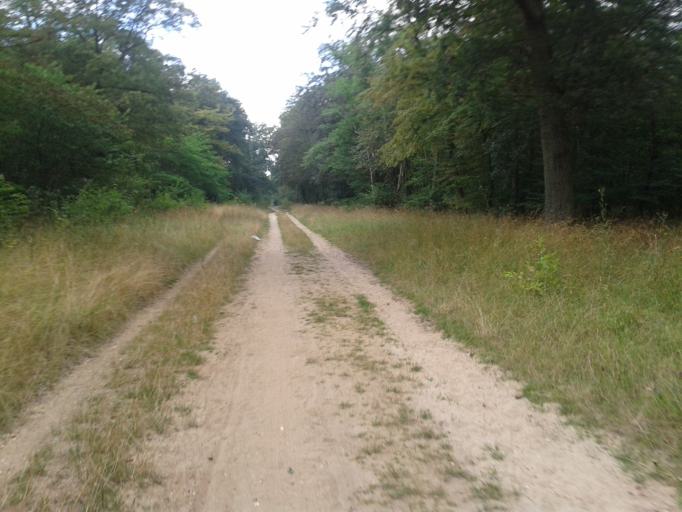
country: FR
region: Ile-de-France
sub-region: Departement des Yvelines
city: Maisons-Laffitte
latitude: 48.9705
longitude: 2.1199
